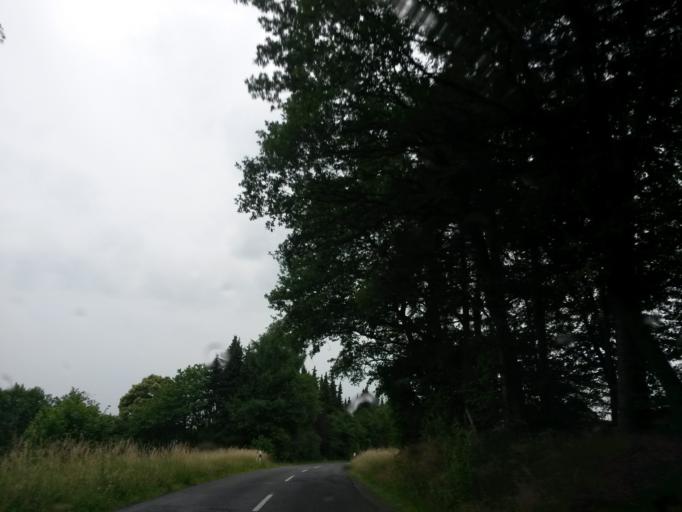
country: DE
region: North Rhine-Westphalia
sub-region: Regierungsbezirk Koln
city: Much
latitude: 50.9234
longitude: 7.3772
